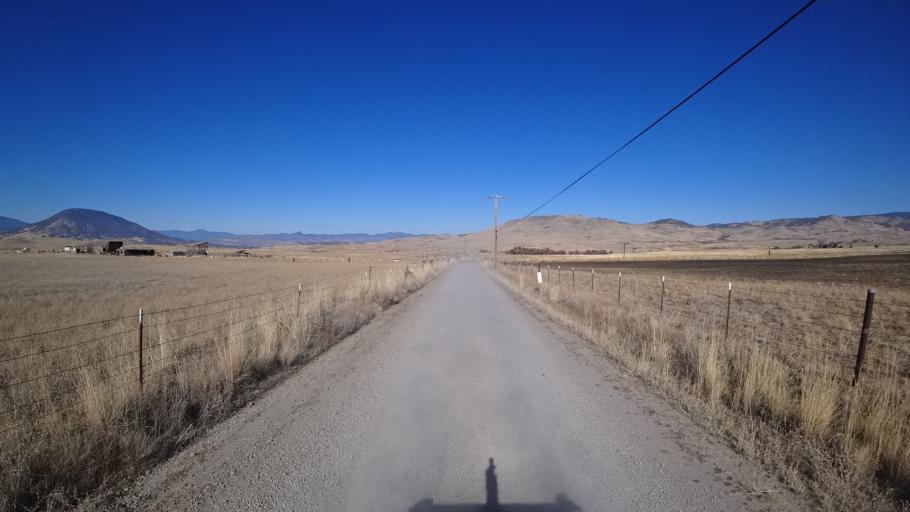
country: US
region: California
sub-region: Siskiyou County
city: Montague
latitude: 41.8032
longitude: -122.4159
